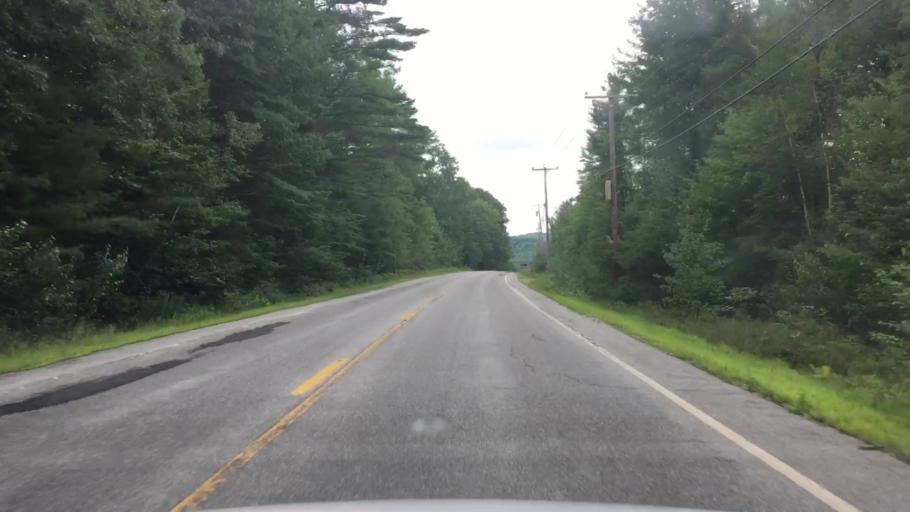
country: US
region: Maine
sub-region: York County
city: Cornish
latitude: 43.8134
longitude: -70.7769
